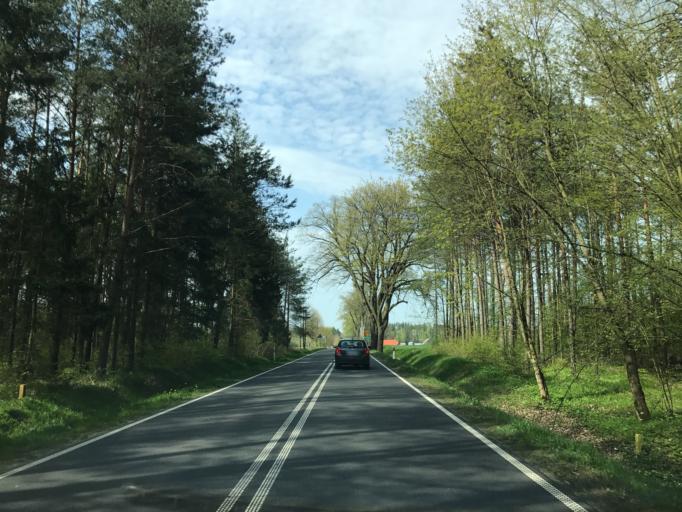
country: PL
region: Warmian-Masurian Voivodeship
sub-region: Powiat dzialdowski
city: Lidzbark
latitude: 53.2883
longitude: 19.8156
